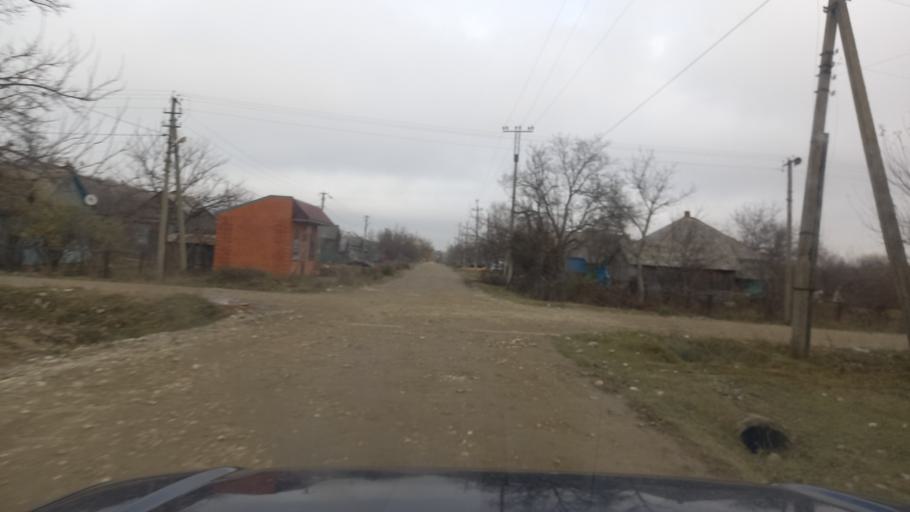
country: RU
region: Krasnodarskiy
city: Neftegorsk
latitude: 44.2495
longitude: 39.7581
